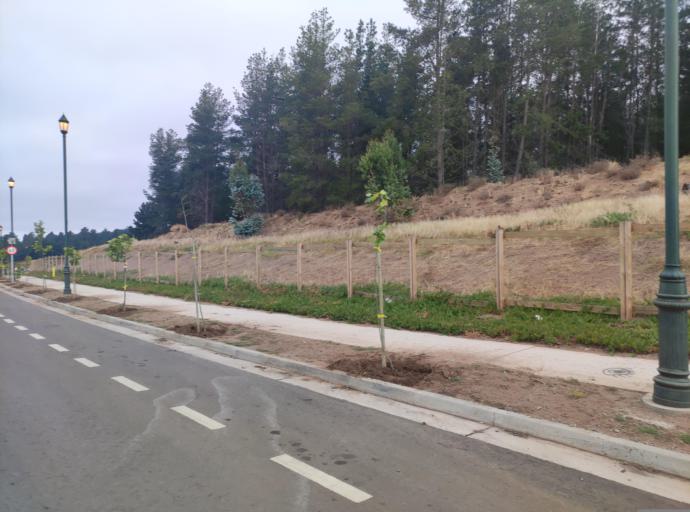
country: CL
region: Valparaiso
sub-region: Provincia de Valparaiso
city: Vina del Mar
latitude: -32.9446
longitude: -71.5304
